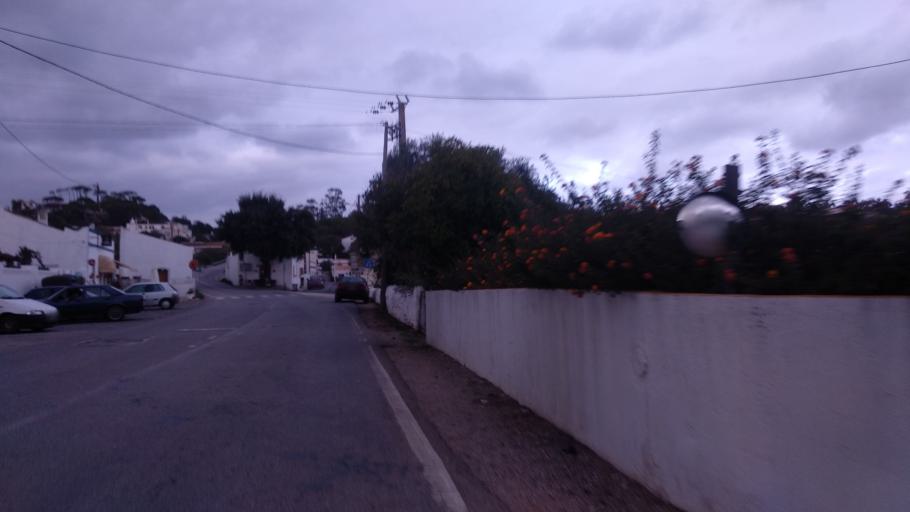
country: PT
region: Faro
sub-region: Sao Bras de Alportel
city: Sao Bras de Alportel
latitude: 37.1744
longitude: -7.9090
